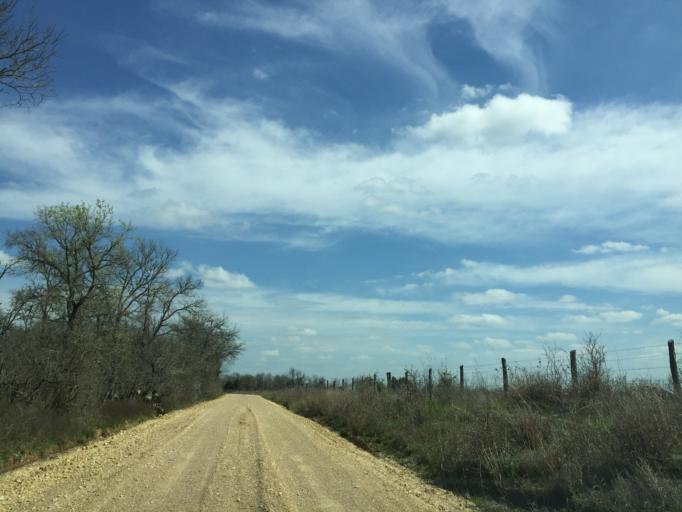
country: US
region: Texas
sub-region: Milam County
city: Thorndale
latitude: 30.5587
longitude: -97.1876
